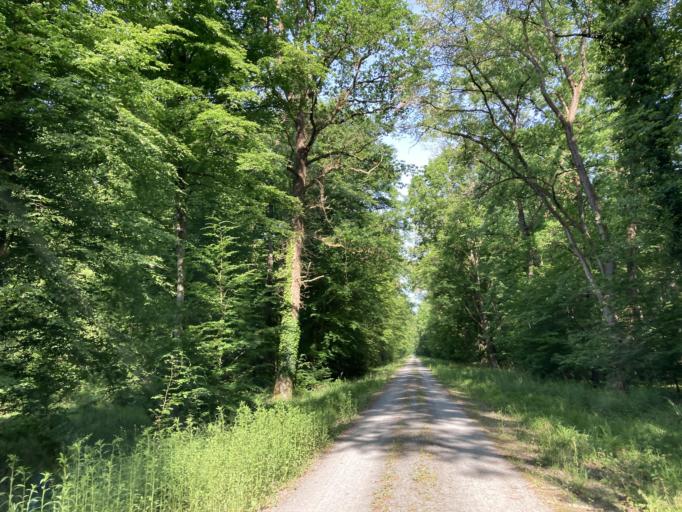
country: DE
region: Baden-Wuerttemberg
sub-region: Karlsruhe Region
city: Hambrucken
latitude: 49.2053
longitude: 8.5836
